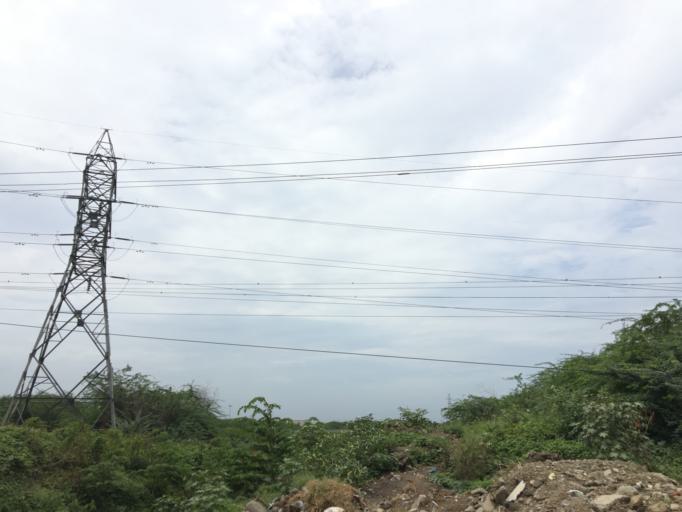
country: IN
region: Tamil Nadu
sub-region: Kancheepuram
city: Madipakkam
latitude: 12.9625
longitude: 80.2156
